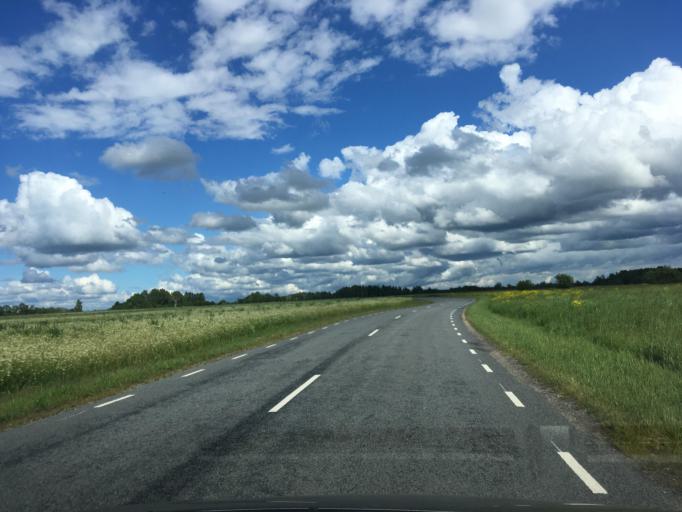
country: EE
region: Paernumaa
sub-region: Halinga vald
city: Parnu-Jaagupi
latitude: 58.6215
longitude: 24.4077
